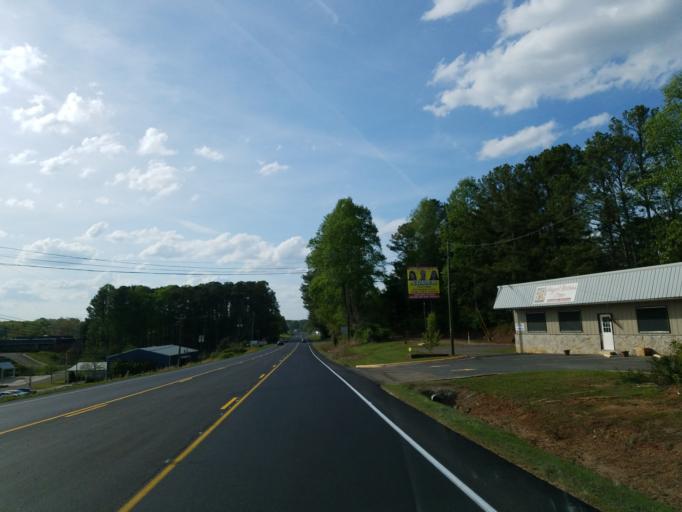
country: US
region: Georgia
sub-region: Pickens County
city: Jasper
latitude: 34.4559
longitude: -84.4091
